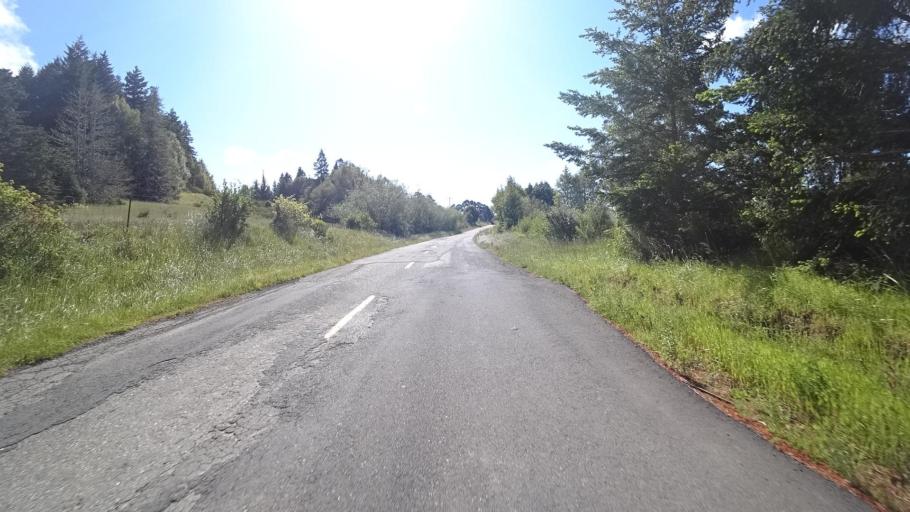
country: US
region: California
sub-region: Humboldt County
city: Ferndale
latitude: 40.3416
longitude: -124.3180
